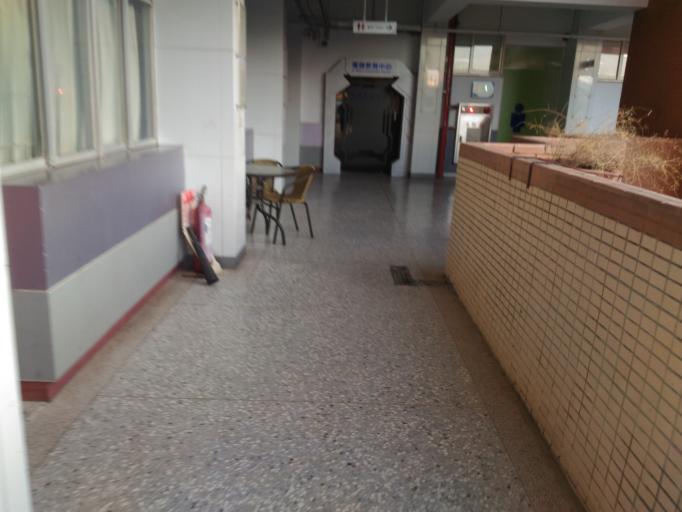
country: TW
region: Taiwan
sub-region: Taichung City
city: Taichung
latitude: 24.1371
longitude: 120.6101
